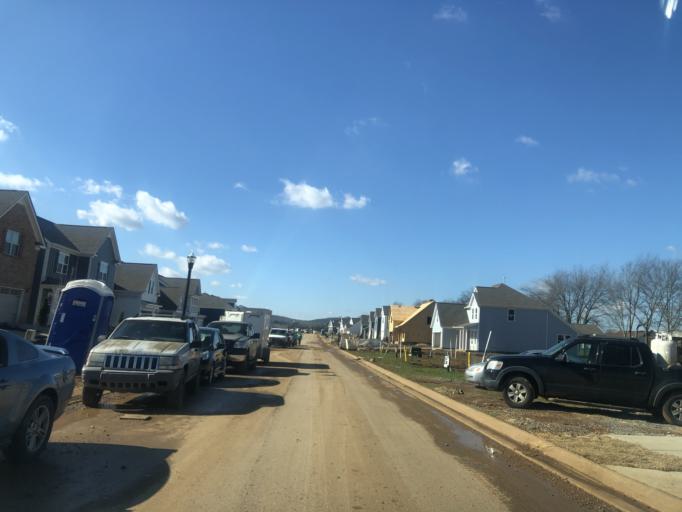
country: US
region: Tennessee
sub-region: Rutherford County
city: Smyrna
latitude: 35.8865
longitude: -86.4852
